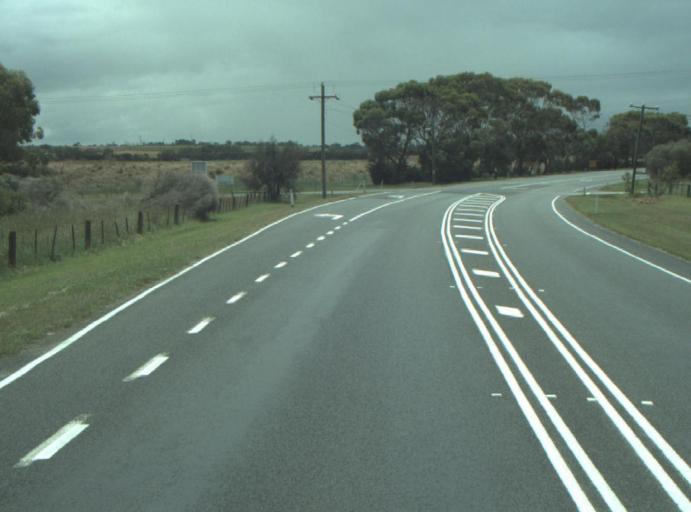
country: AU
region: Victoria
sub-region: Greater Geelong
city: Wandana Heights
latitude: -38.2284
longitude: 144.2802
